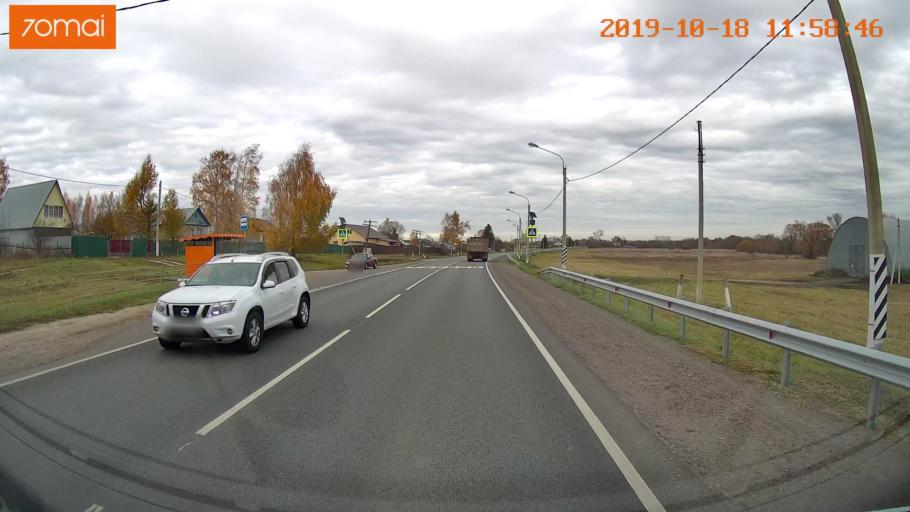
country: RU
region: Rjazan
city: Zakharovo
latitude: 54.2750
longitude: 39.1695
